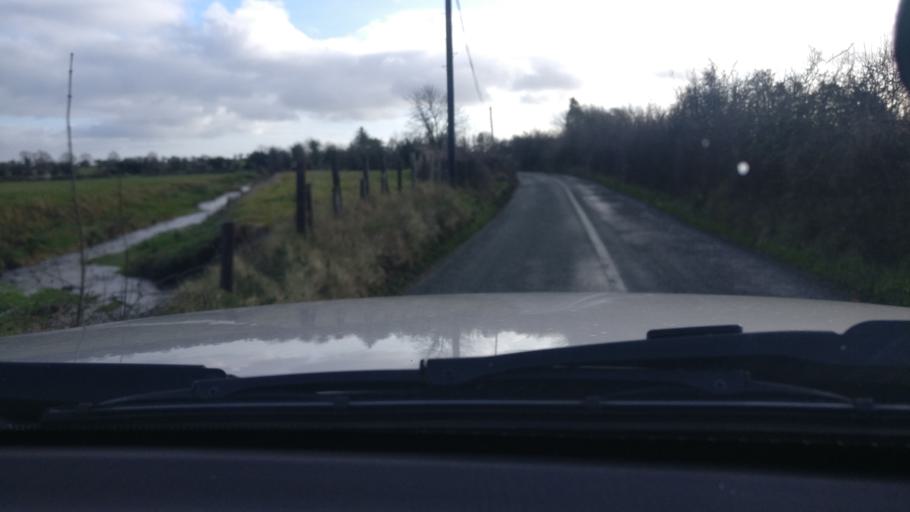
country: IE
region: Connaught
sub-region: County Galway
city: Ballinasloe
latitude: 53.2262
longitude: -8.2927
